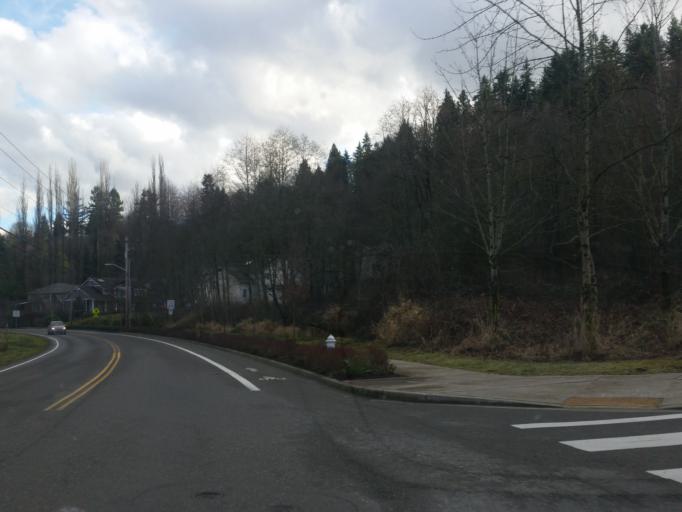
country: US
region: Washington
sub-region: King County
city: Bothell
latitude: 47.7538
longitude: -122.1962
